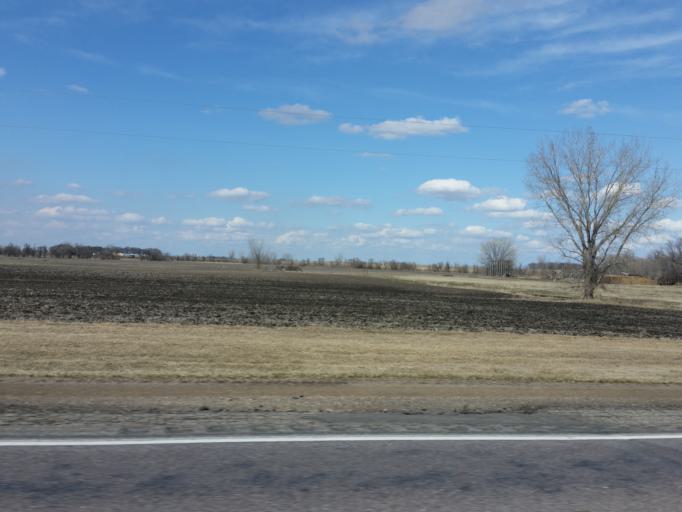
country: US
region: Minnesota
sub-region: Lac qui Parle County
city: Madison
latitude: 44.9360
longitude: -96.2030
